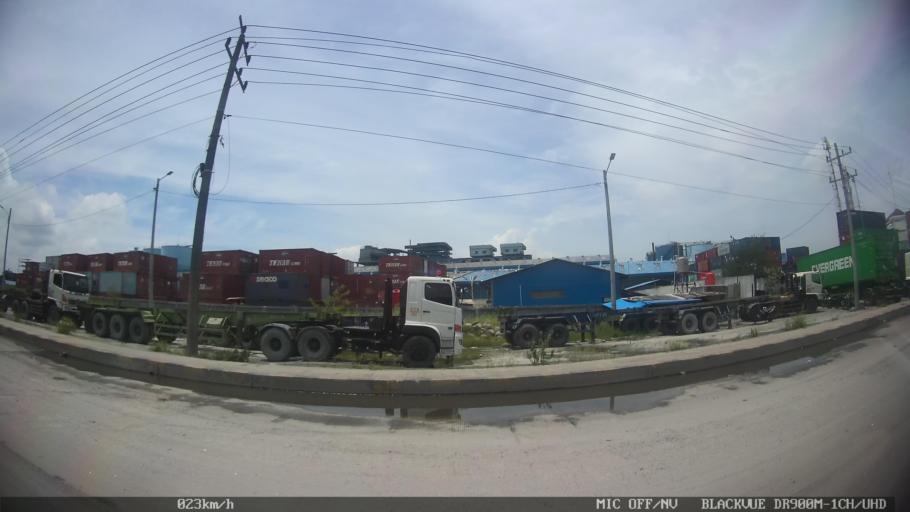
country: ID
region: North Sumatra
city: Belawan
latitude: 3.7810
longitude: 98.6961
